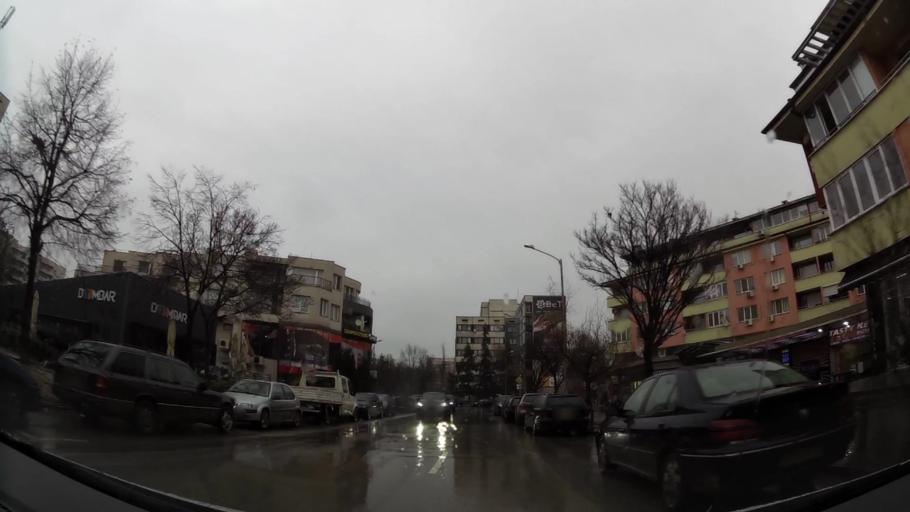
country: BG
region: Sofia-Capital
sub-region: Stolichna Obshtina
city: Sofia
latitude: 42.6530
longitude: 23.3426
